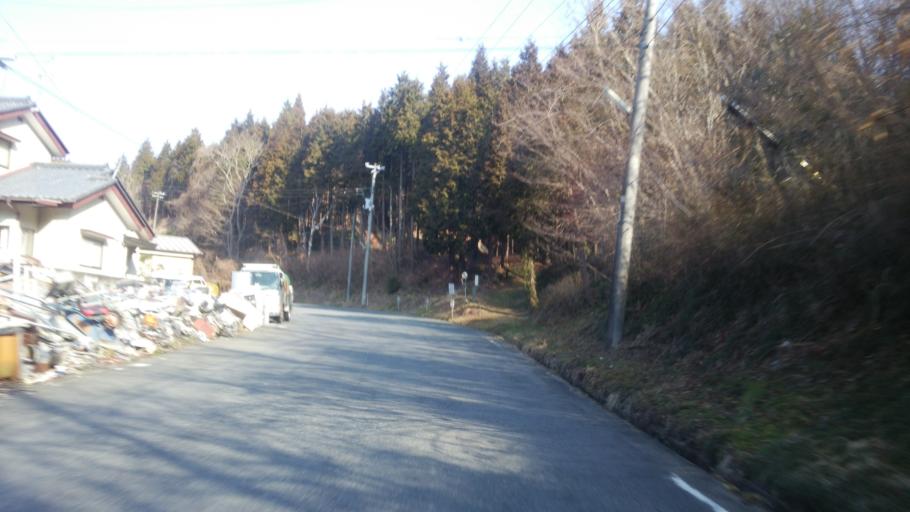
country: JP
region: Fukushima
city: Iwaki
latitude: 37.0183
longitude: 140.8164
